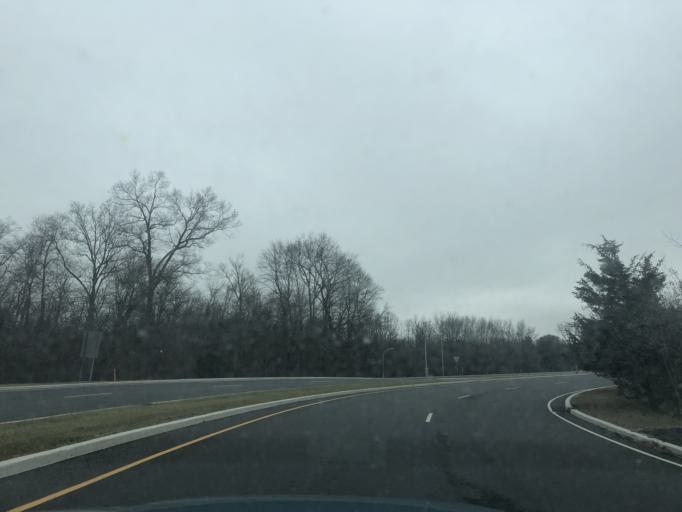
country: US
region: New Jersey
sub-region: Somerset County
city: Kingston
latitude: 40.3573
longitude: -74.6044
